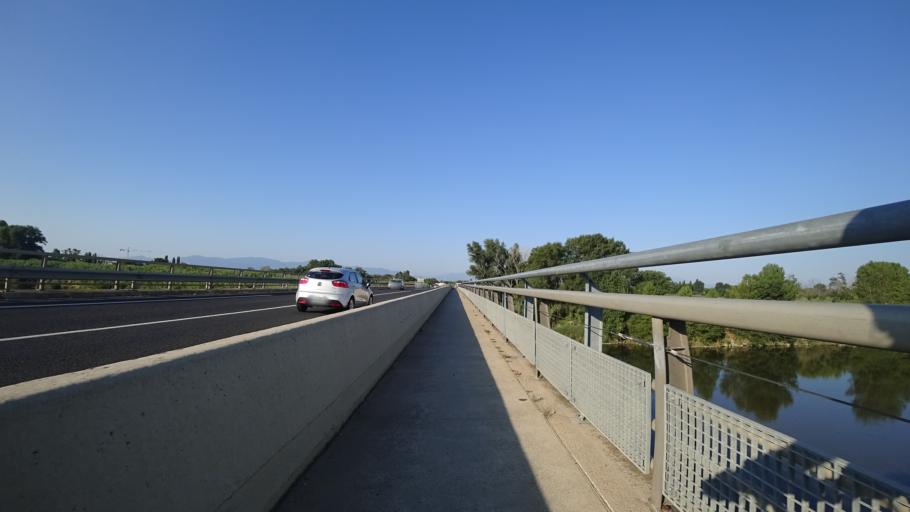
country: FR
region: Languedoc-Roussillon
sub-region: Departement des Pyrenees-Orientales
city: Canet-en-Roussillon
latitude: 42.7113
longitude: 3.0234
